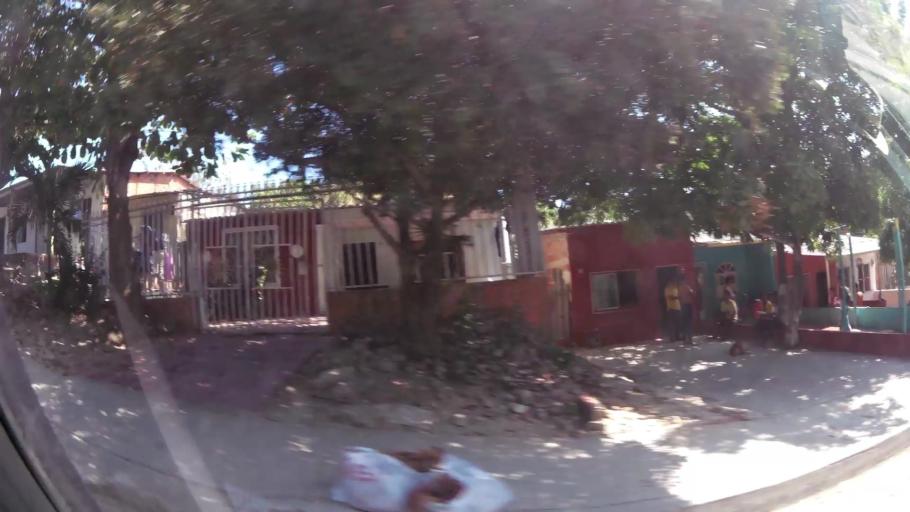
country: CO
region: Atlantico
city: Barranquilla
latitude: 10.9773
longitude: -74.8254
